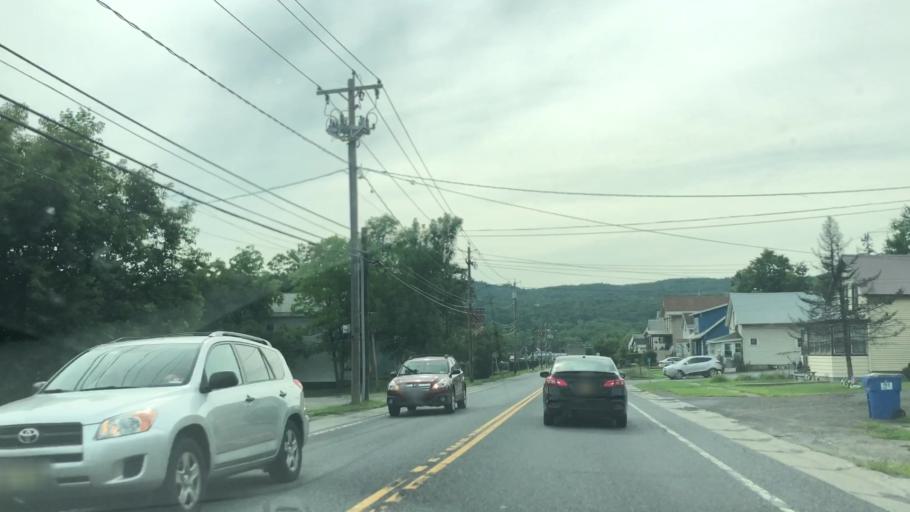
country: US
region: New York
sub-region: Washington County
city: Whitehall
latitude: 43.5501
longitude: -73.3932
